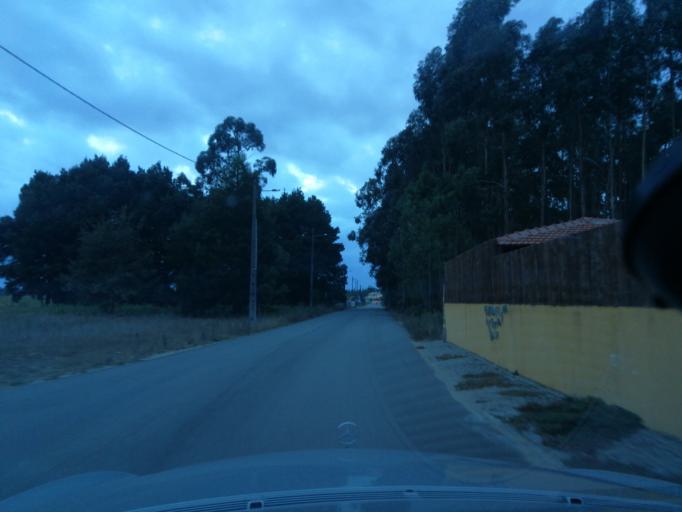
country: PT
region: Aveiro
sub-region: Estarreja
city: Estarreja
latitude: 40.7649
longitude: -8.5908
